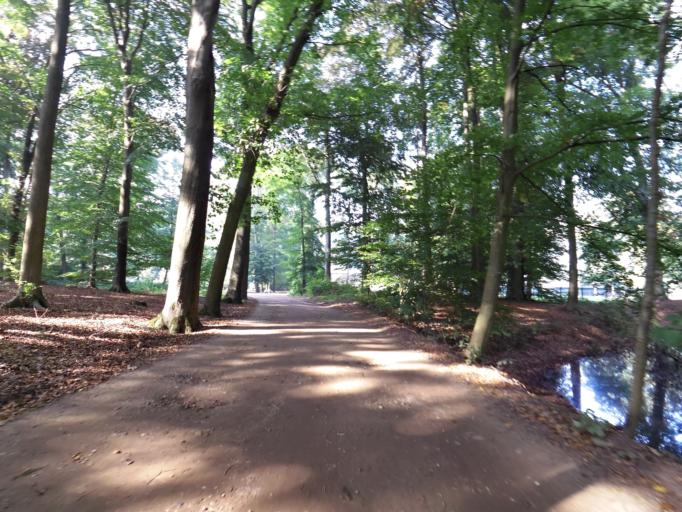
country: NL
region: Gelderland
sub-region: Gemeente Doesburg
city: Doesburg
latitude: 51.9483
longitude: 6.1962
